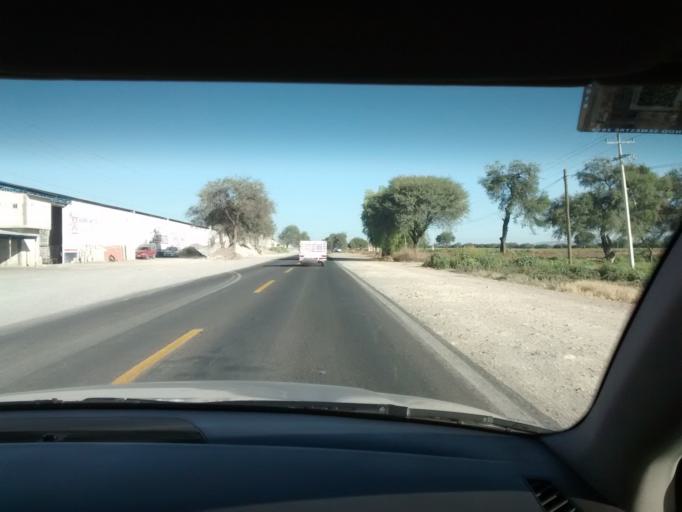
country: MX
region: Puebla
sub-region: Santiago Miahuatlan
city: San Jose Monte Chiquito
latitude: 18.5019
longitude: -97.4786
